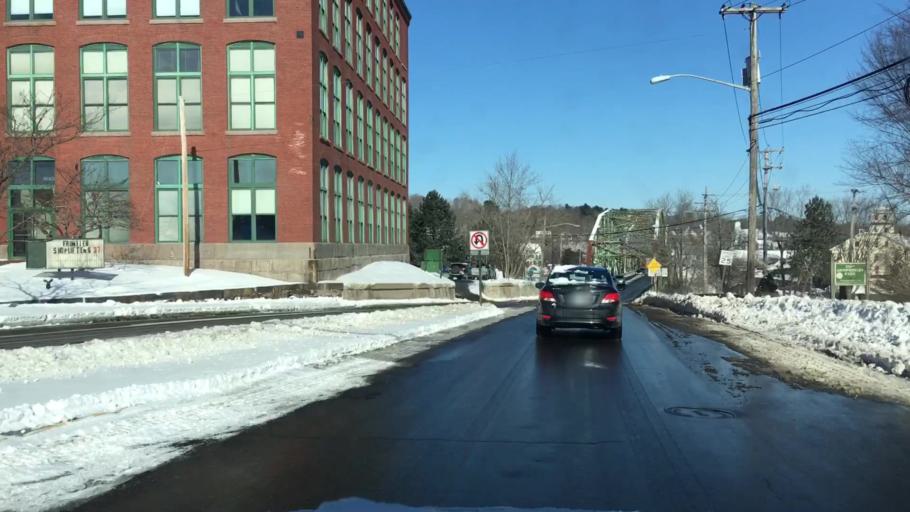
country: US
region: Maine
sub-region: Cumberland County
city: Brunswick
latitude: 43.9188
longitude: -69.9666
